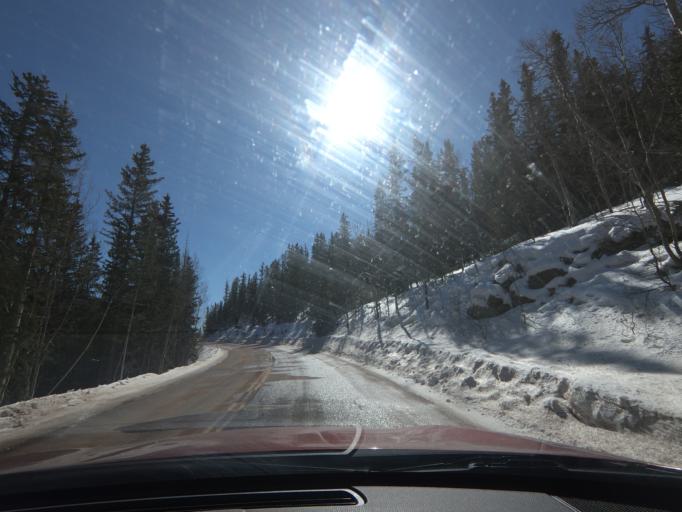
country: US
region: Colorado
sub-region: Teller County
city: Cripple Creek
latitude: 38.7492
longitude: -105.1019
